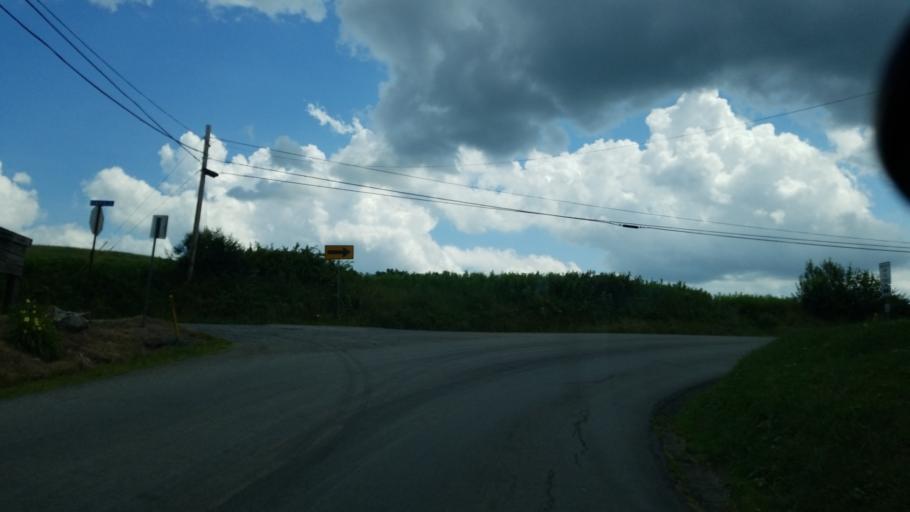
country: US
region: Pennsylvania
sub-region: Jefferson County
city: Brookville
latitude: 41.2387
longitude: -79.0108
